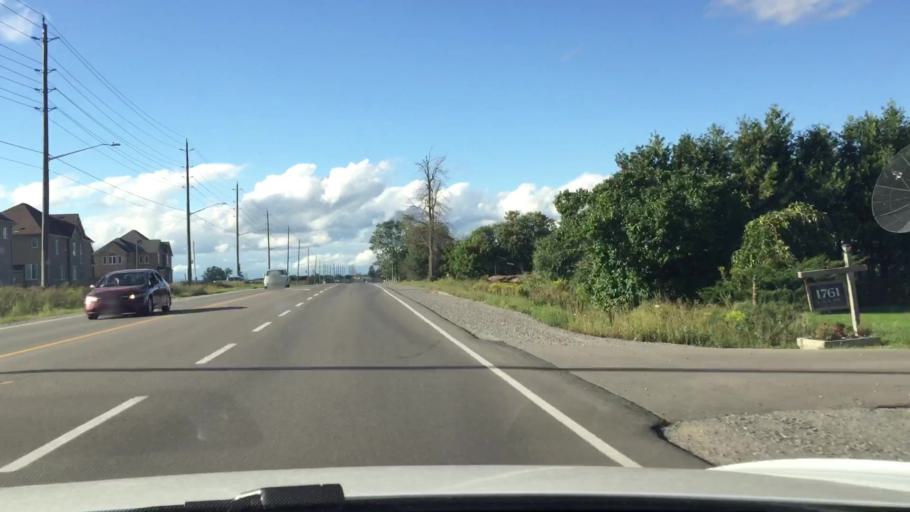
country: CA
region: Ontario
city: Oshawa
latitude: 43.9504
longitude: -78.8543
